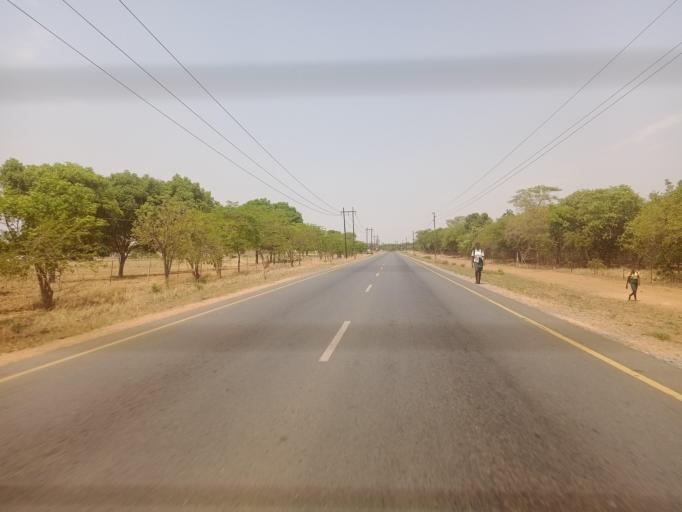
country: ZM
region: Lusaka
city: Lusaka
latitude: -15.2800
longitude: 28.3948
